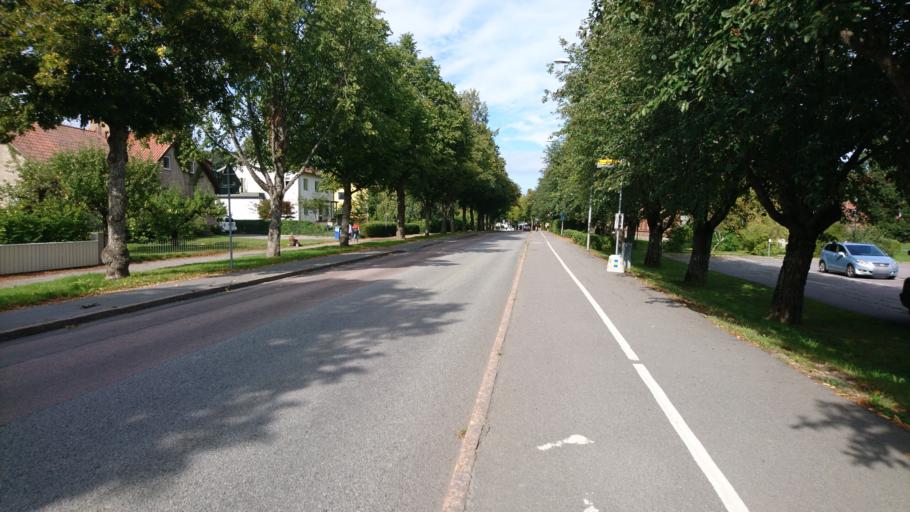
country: SE
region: Uppsala
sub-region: Uppsala Kommun
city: Uppsala
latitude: 59.8484
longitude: 17.6224
